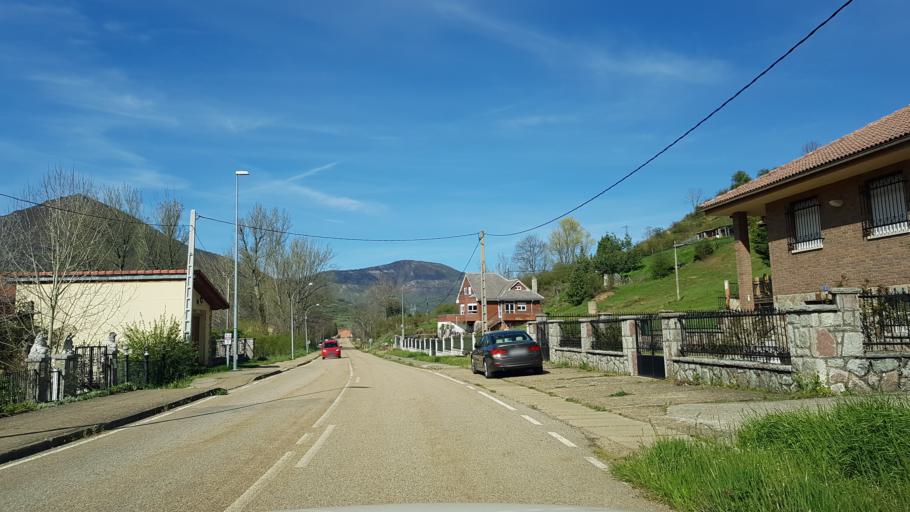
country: ES
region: Castille and Leon
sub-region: Provincia de Leon
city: Villamanin
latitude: 42.9415
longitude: -5.6465
